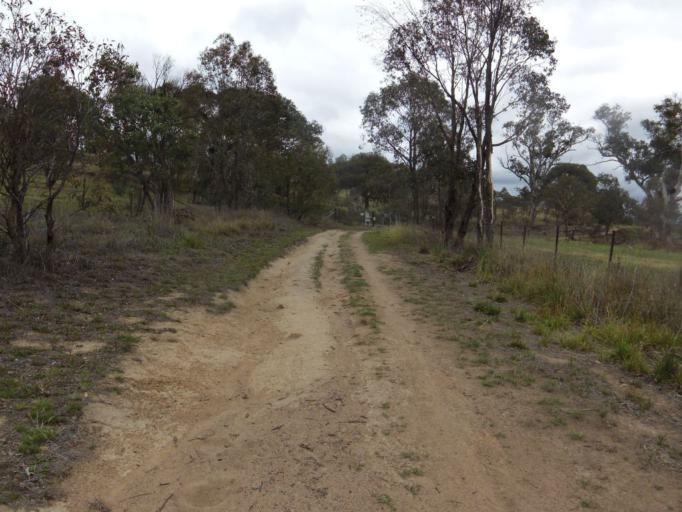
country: AU
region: Australian Capital Territory
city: Macquarie
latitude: -35.3497
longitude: 149.0236
